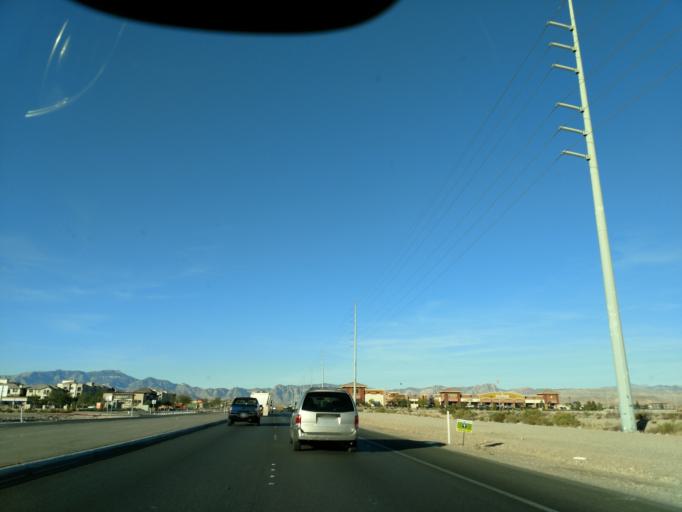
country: US
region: Nevada
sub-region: Clark County
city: Enterprise
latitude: 36.0203
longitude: -115.2630
